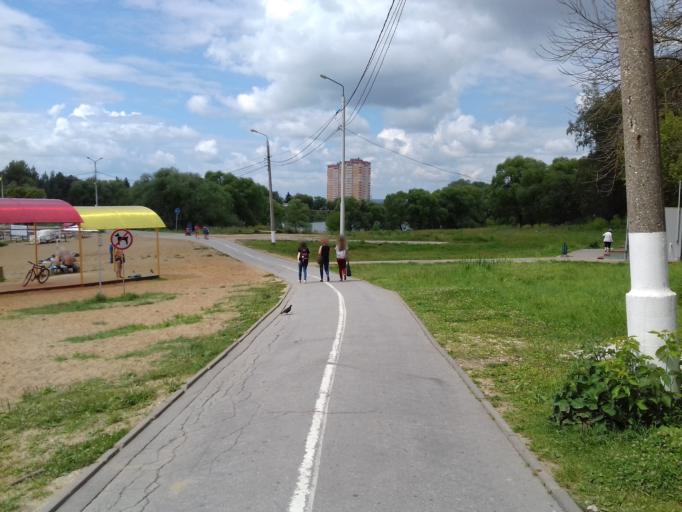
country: RU
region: Tula
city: Tula
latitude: 54.1831
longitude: 37.5810
